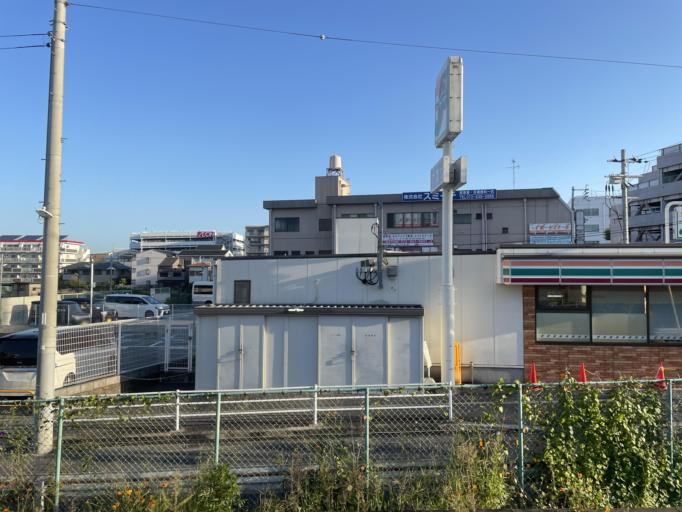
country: JP
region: Osaka
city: Kashihara
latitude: 34.5717
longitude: 135.5924
